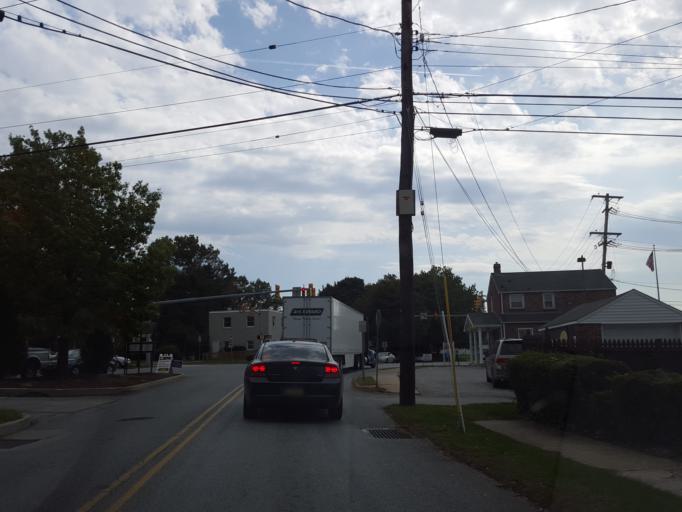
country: US
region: Pennsylvania
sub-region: York County
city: East York
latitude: 39.9680
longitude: -76.7003
